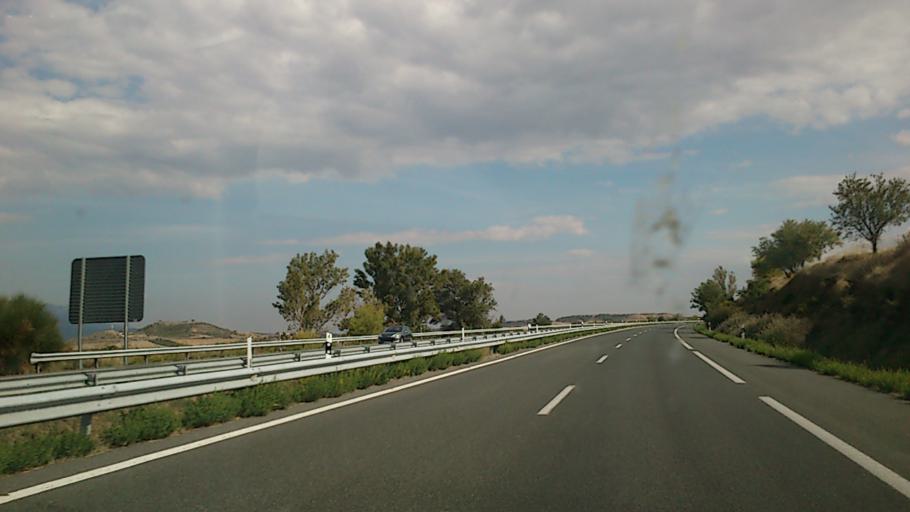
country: ES
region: La Rioja
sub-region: Provincia de La Rioja
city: Ollauri
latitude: 42.5510
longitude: -2.8553
